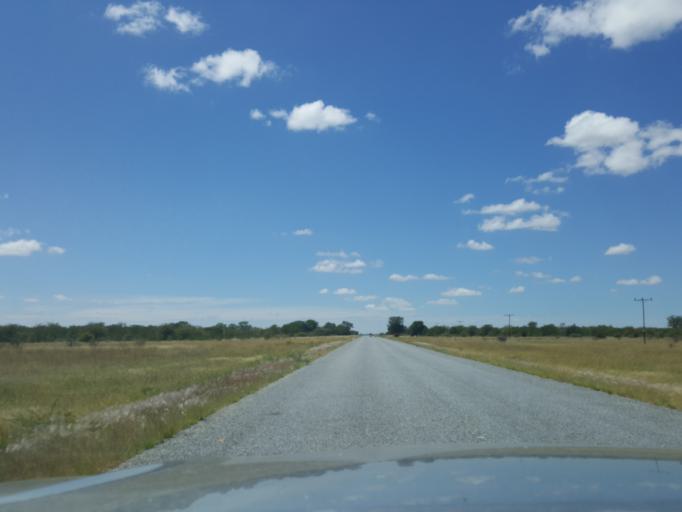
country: BW
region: Central
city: Gweta
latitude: -20.1343
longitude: 25.6509
